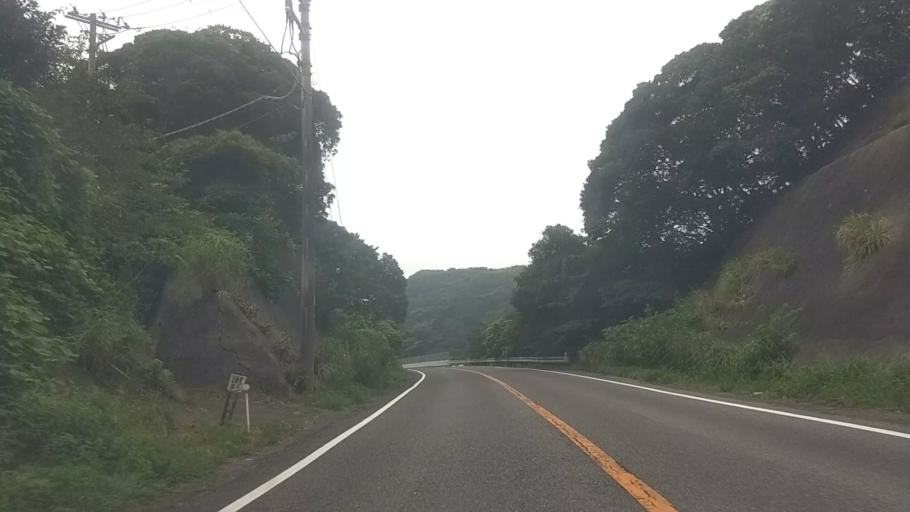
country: JP
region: Chiba
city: Katsuura
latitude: 35.1556
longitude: 140.3067
